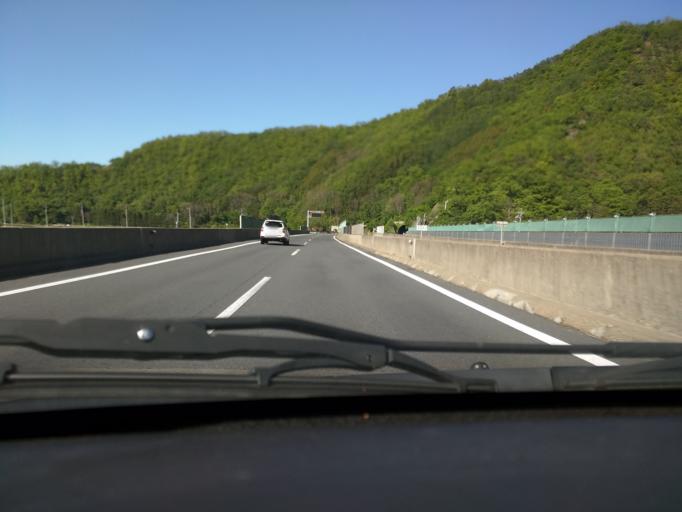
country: JP
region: Nagano
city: Suzaka
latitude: 36.6133
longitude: 138.2568
